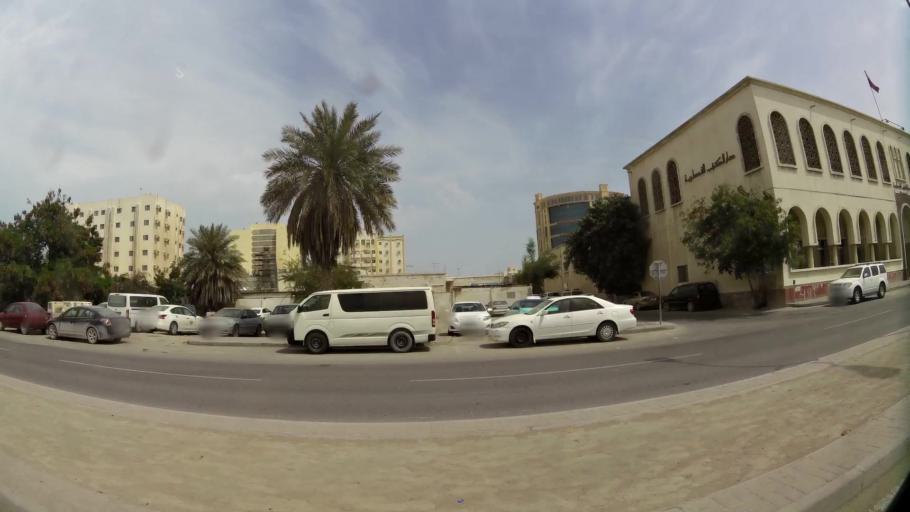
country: QA
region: Baladiyat ad Dawhah
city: Doha
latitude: 25.2830
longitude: 51.5400
